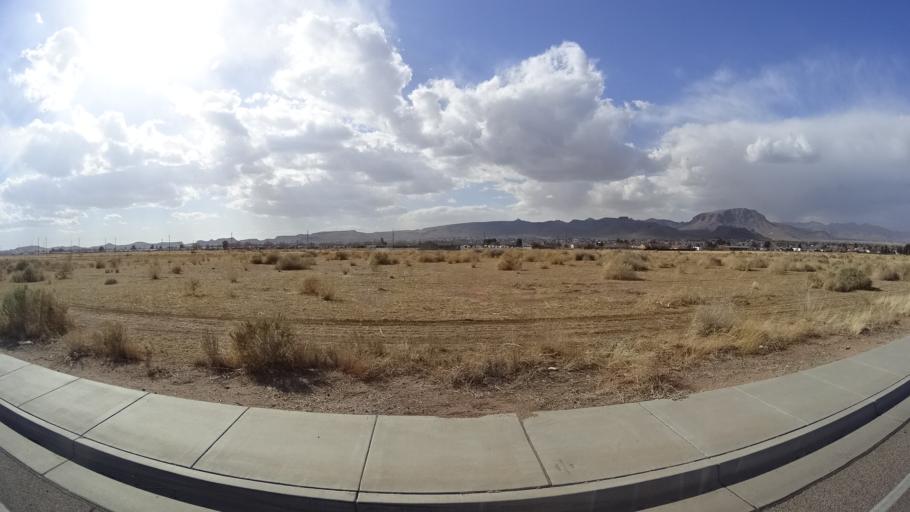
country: US
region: Arizona
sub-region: Mohave County
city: New Kingman-Butler
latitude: 35.2349
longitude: -114.0118
